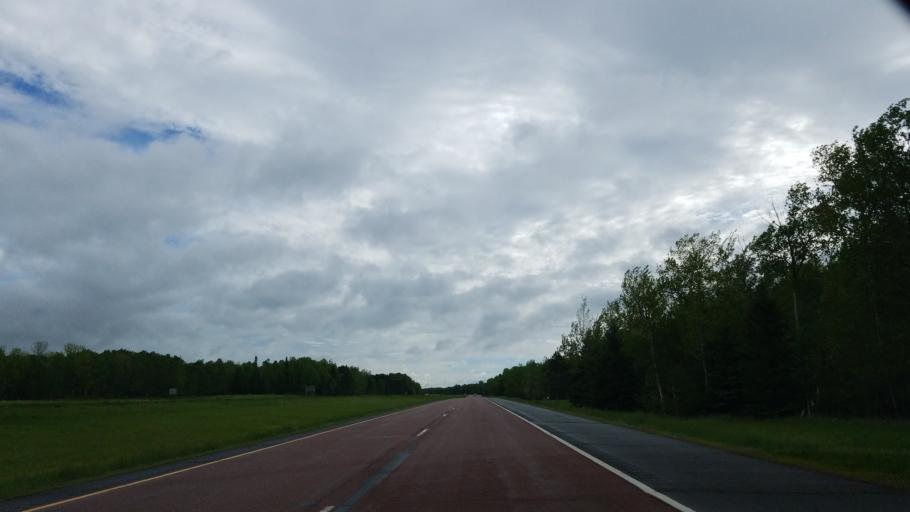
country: US
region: Minnesota
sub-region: Saint Louis County
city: Arnold
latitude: 46.8904
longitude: -91.9187
